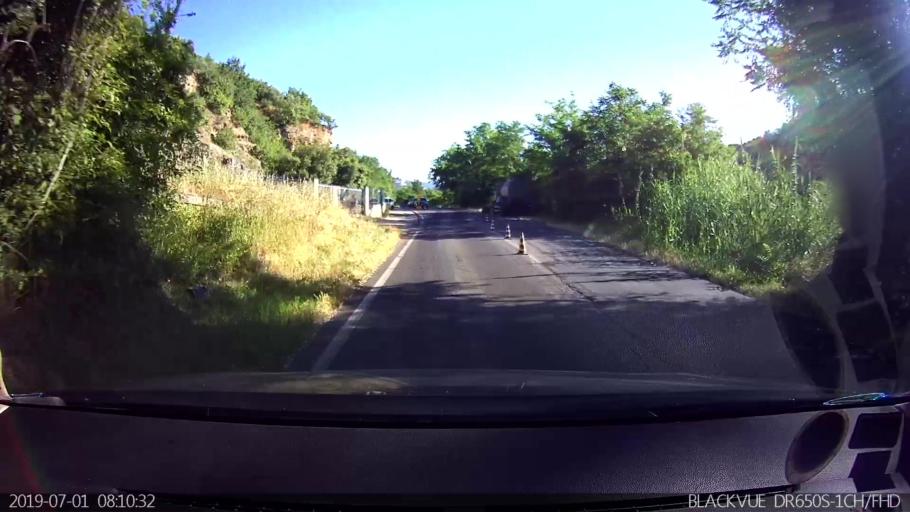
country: IT
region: Latium
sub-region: Provincia di Frosinone
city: Sant'Angelo in Villa-Giglio
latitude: 41.6705
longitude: 13.4216
